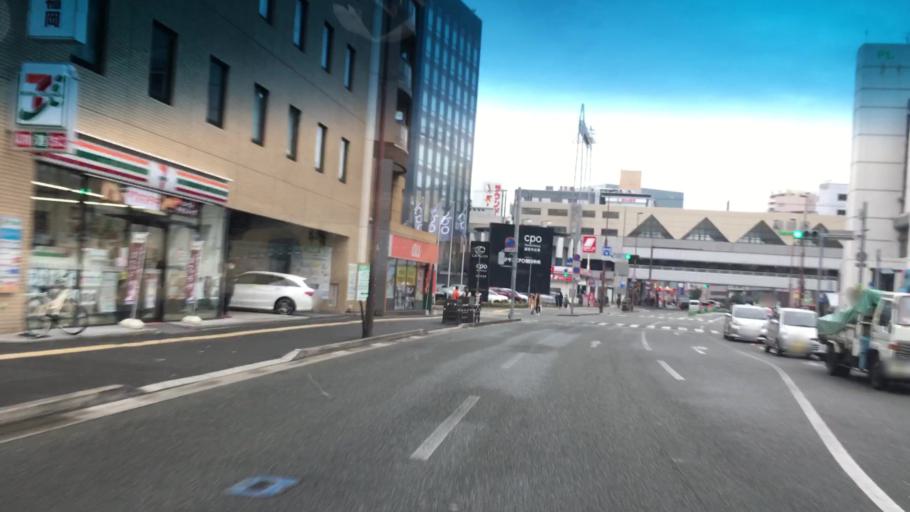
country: JP
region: Fukuoka
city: Fukuoka-shi
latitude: 33.5816
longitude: 130.4034
